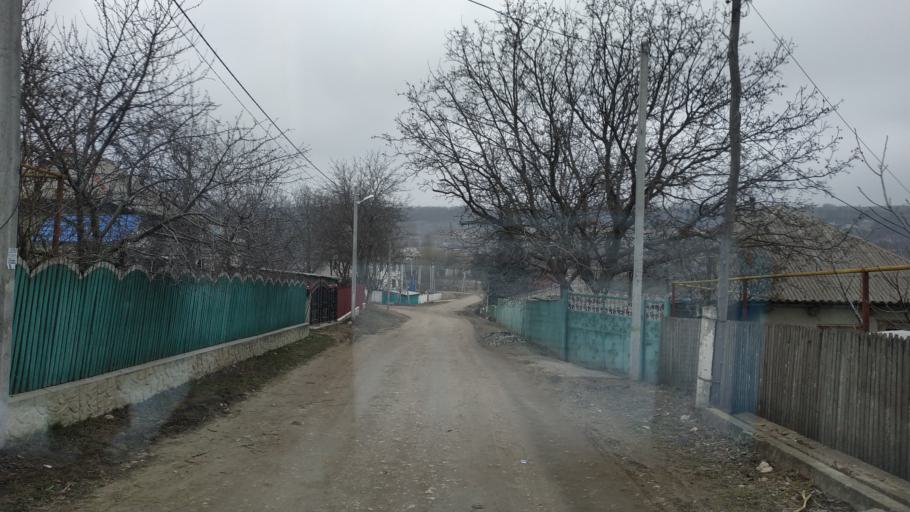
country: MD
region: Hincesti
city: Hincesti
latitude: 46.9792
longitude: 28.4736
